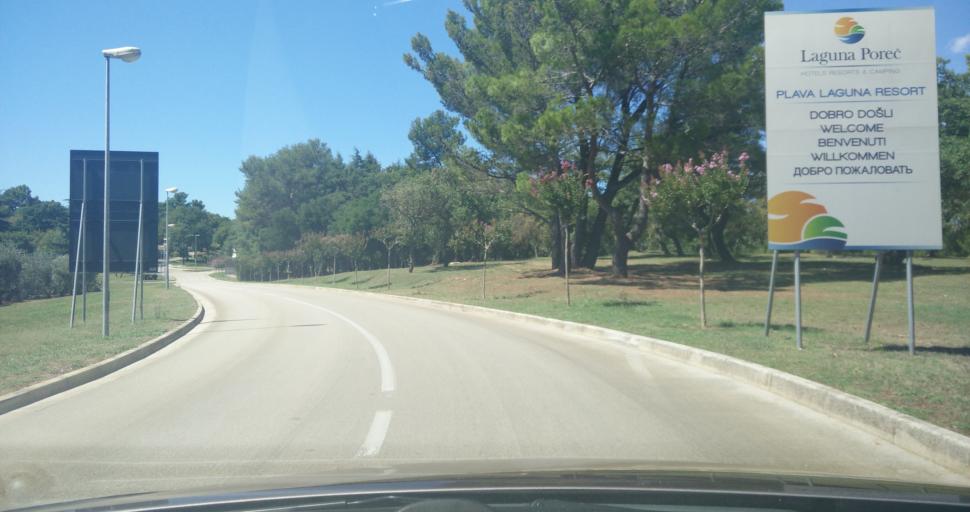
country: HR
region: Istarska
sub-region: Grad Porec
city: Porec
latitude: 45.2113
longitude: 13.5996
